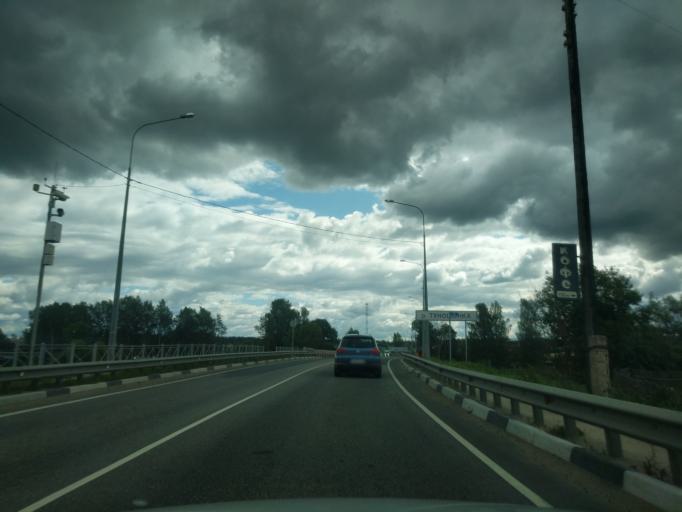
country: RU
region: Jaroslavl
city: Tunoshna
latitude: 57.5433
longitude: 40.1157
